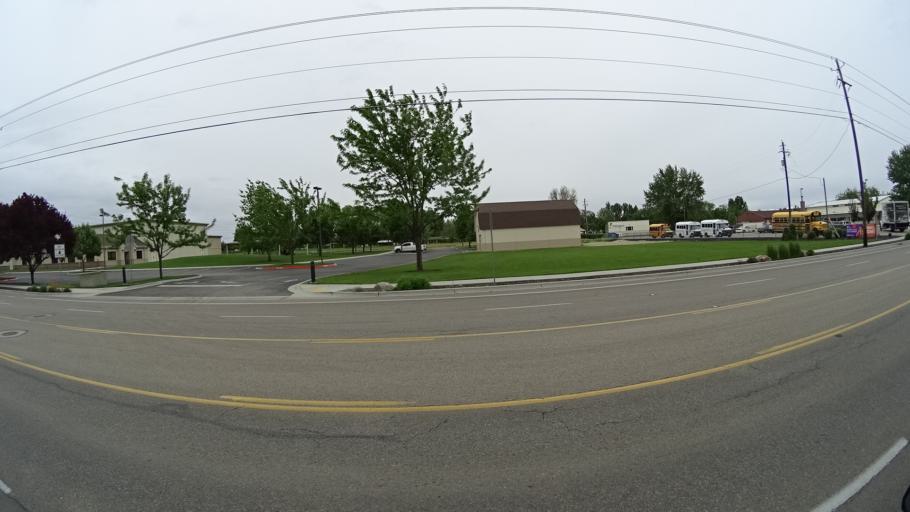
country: US
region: Idaho
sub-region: Ada County
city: Meridian
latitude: 43.6340
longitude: -116.3365
